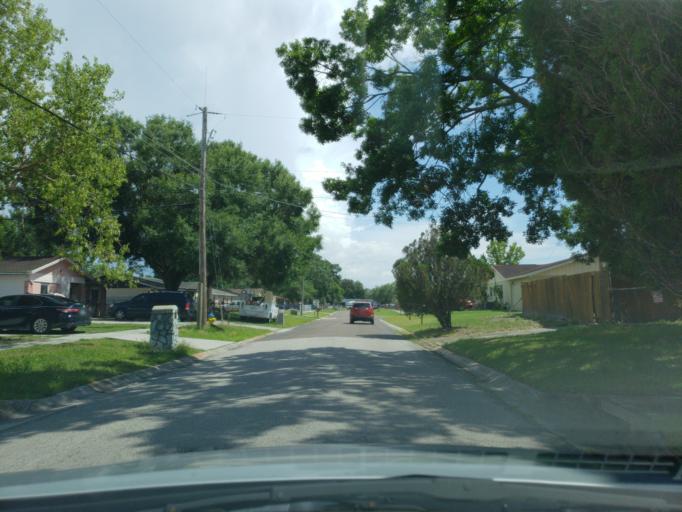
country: US
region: Florida
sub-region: Hillsborough County
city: Palm River-Clair Mel
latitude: 27.9323
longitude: -82.3763
